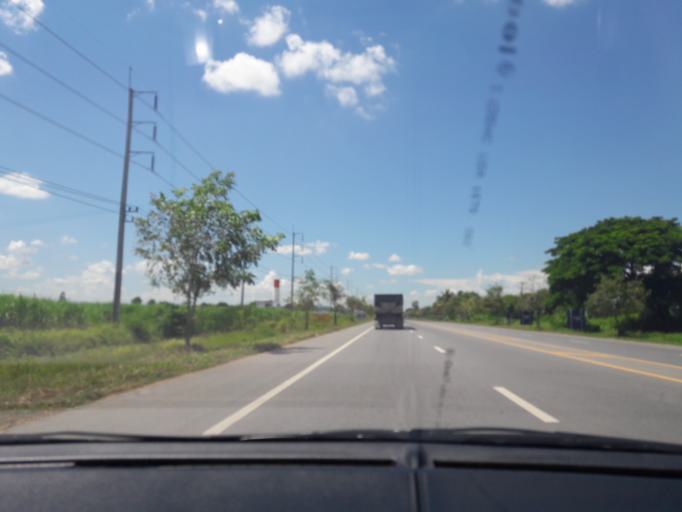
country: TH
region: Kanchanaburi
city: Phanom Thuan
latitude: 14.0474
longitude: 99.7817
